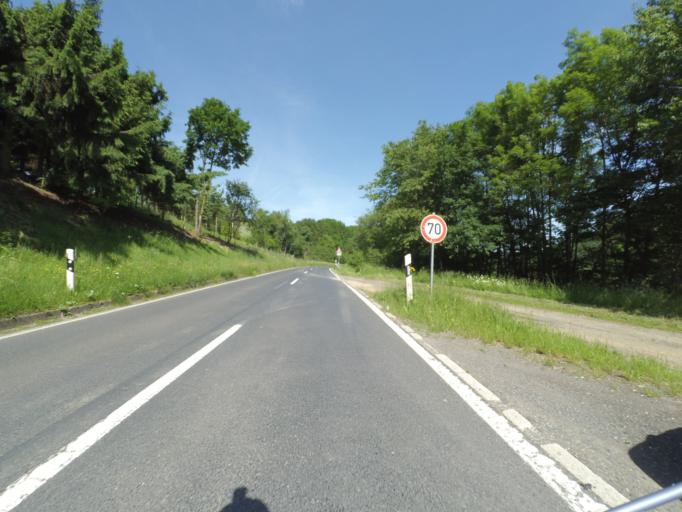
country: DE
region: Rheinland-Pfalz
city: Kalenborn
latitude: 50.2643
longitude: 7.0739
